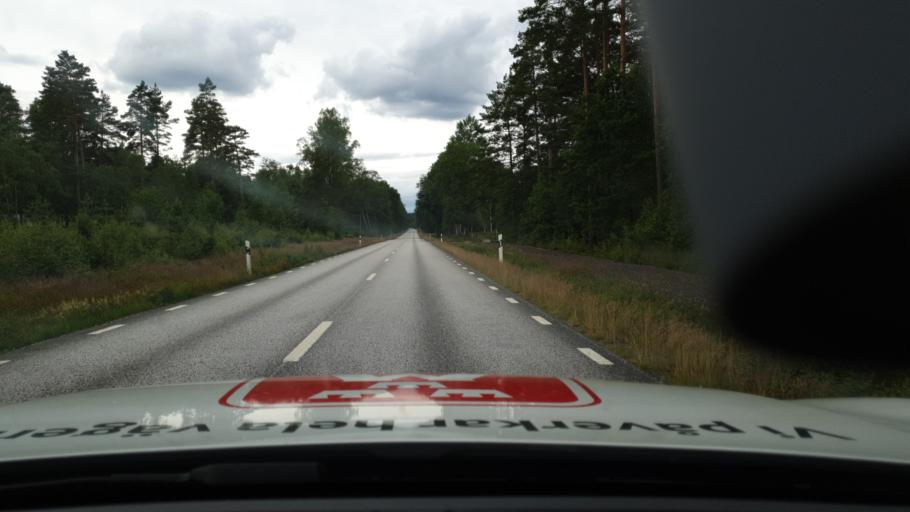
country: SE
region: Joenkoeping
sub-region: Gnosjo Kommun
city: Hillerstorp
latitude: 57.2845
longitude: 13.8228
